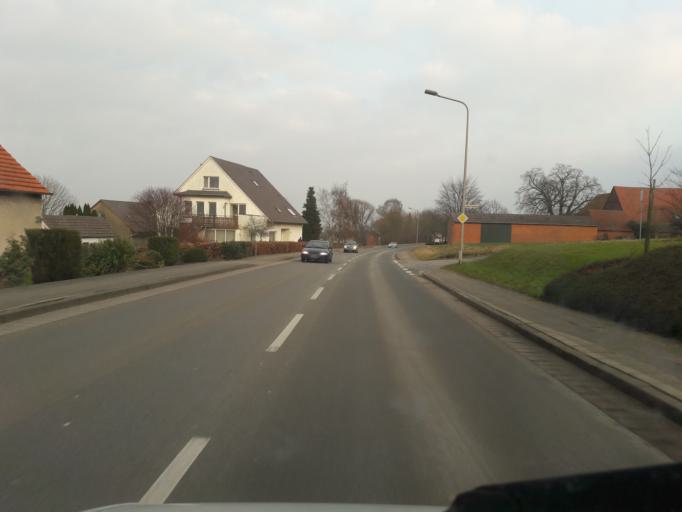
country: DE
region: North Rhine-Westphalia
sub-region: Regierungsbezirk Detmold
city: Hille
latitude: 52.2902
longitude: 8.7310
